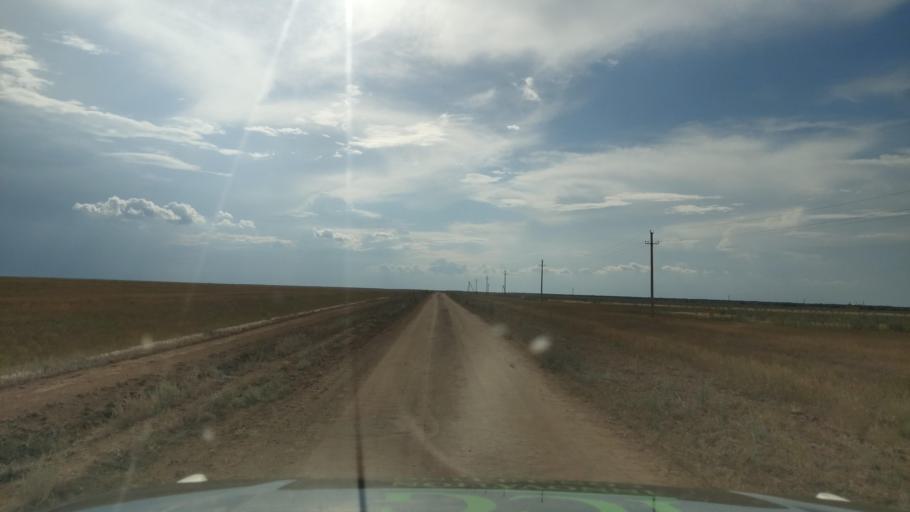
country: KZ
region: Pavlodar
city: Pavlodar
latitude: 52.5089
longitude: 77.5608
